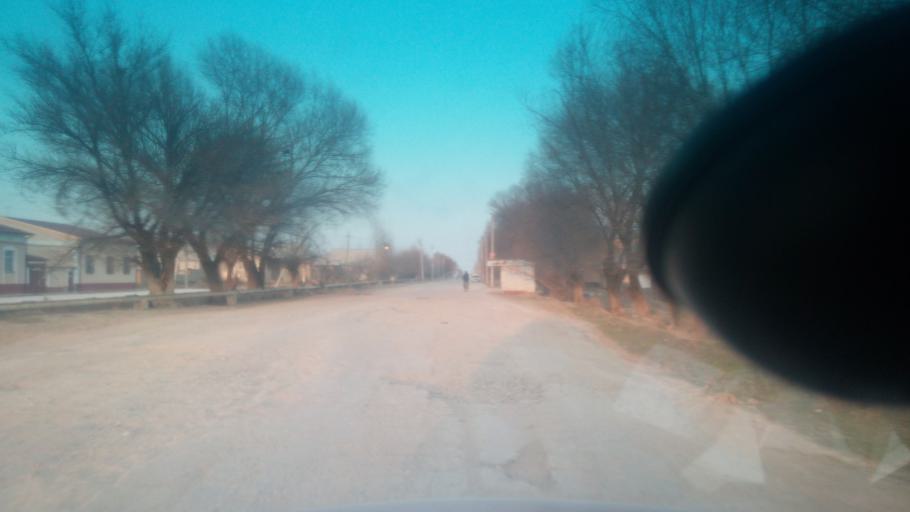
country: UZ
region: Sirdaryo
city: Guliston
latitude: 40.5245
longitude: 68.7755
